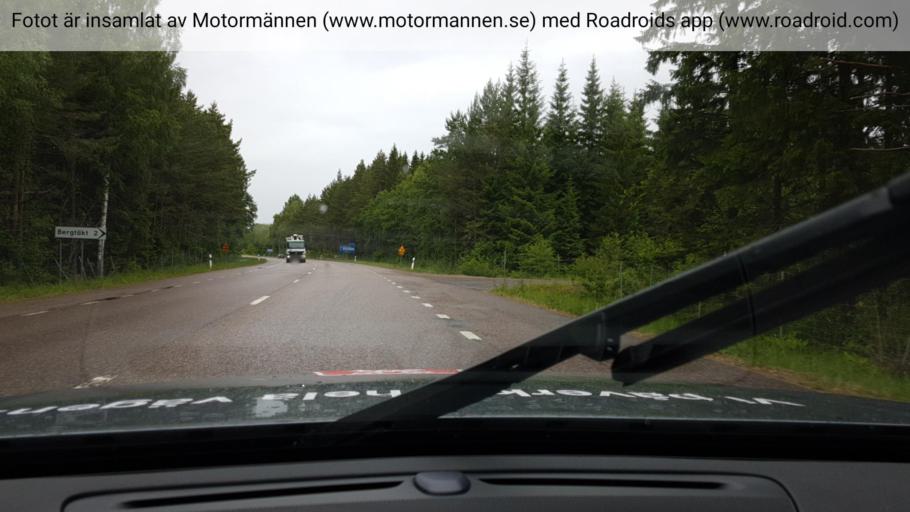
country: SE
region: Uppsala
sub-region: Alvkarleby Kommun
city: AElvkarleby
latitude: 60.5968
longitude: 17.4615
